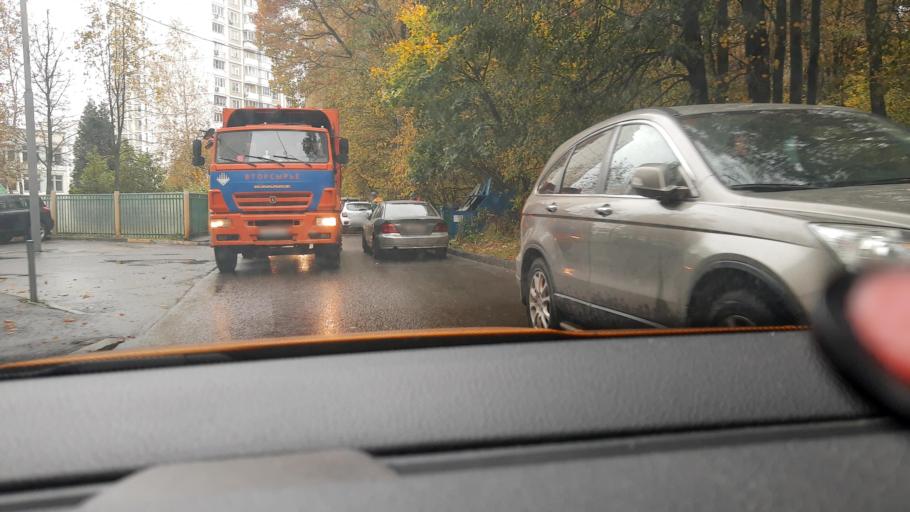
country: RU
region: Moskovskaya
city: Krasnogorsk
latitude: 55.8448
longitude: 37.3431
